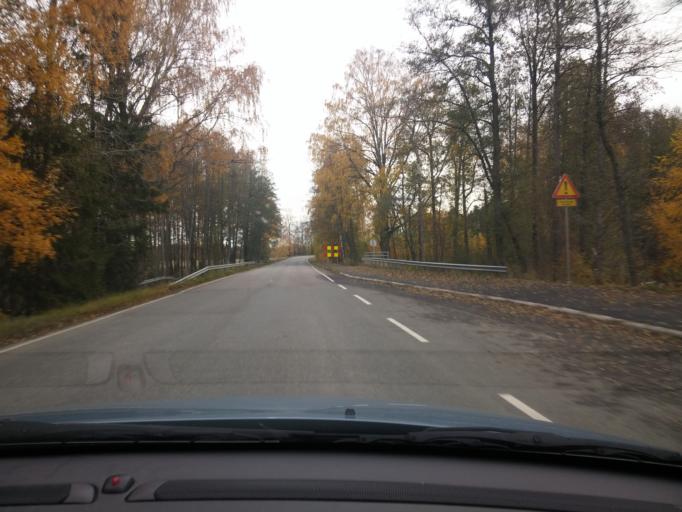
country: FI
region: Haeme
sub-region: Forssa
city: Tammela
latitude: 60.7921
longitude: 23.8173
